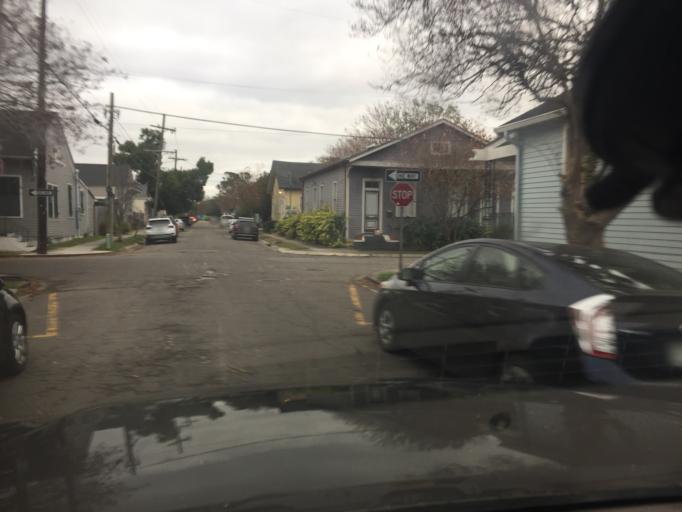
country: US
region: Louisiana
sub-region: Orleans Parish
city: New Orleans
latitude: 29.9804
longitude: -90.0820
